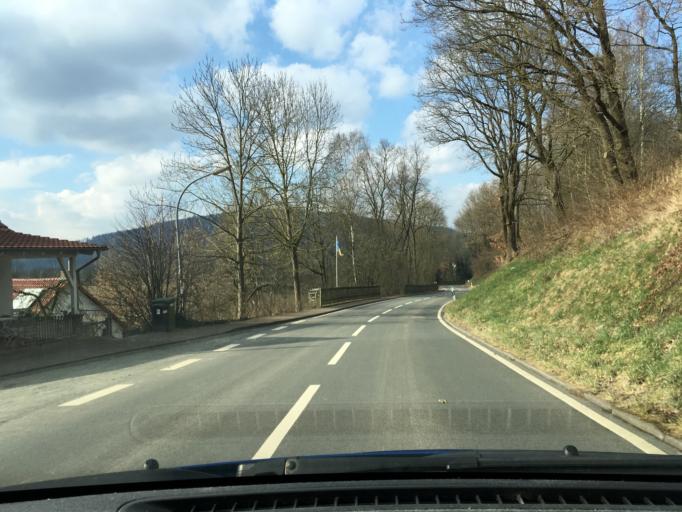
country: DE
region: Lower Saxony
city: Uslar
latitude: 51.6190
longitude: 9.6224
